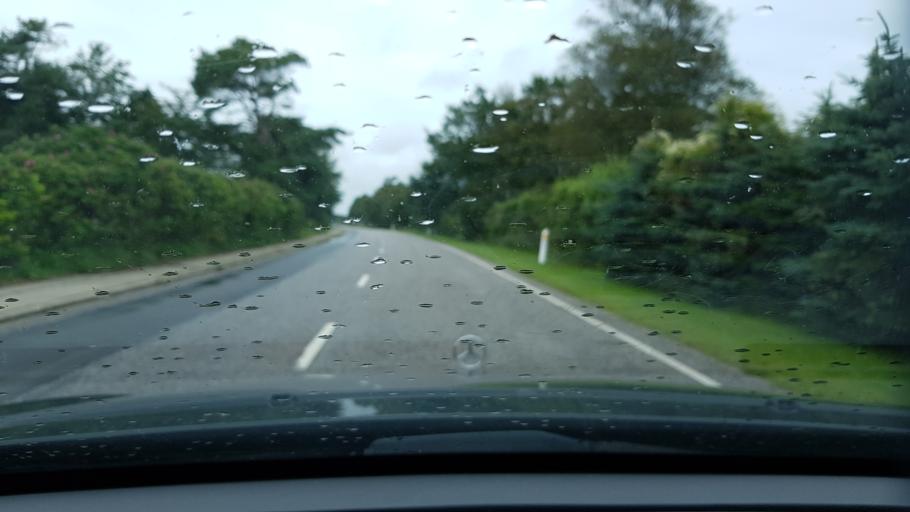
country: DK
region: North Denmark
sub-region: Alborg Kommune
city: Hals
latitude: 56.8166
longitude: 10.2710
